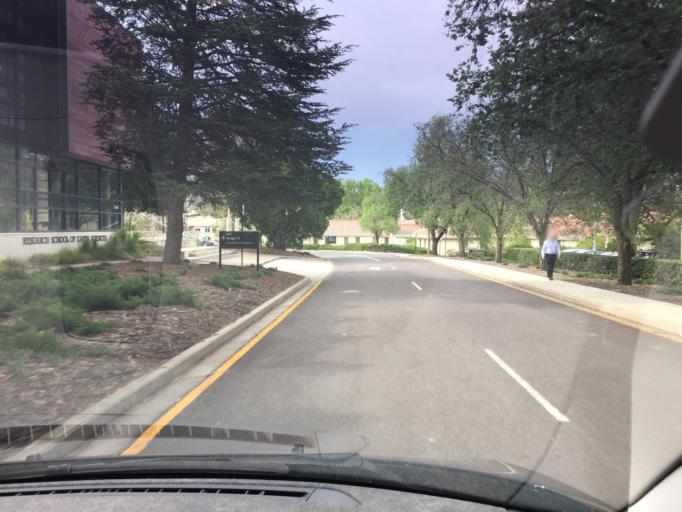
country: AU
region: Australian Capital Territory
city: Acton
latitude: -35.2842
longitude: 149.1156
